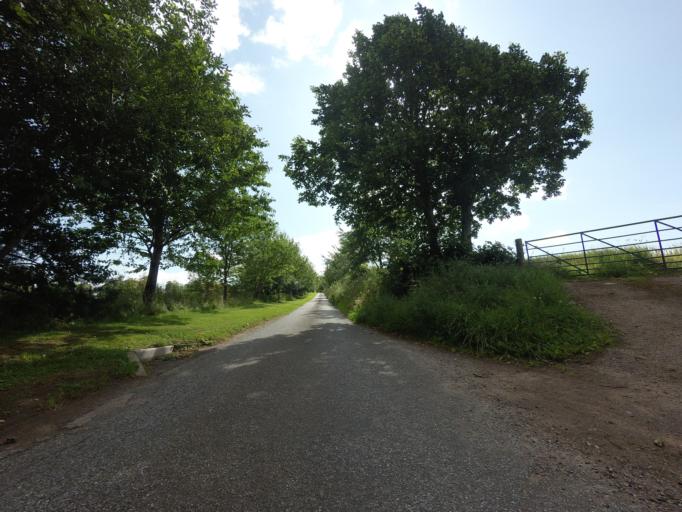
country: GB
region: Scotland
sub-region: Highland
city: Nairn
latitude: 57.5528
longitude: -3.8643
